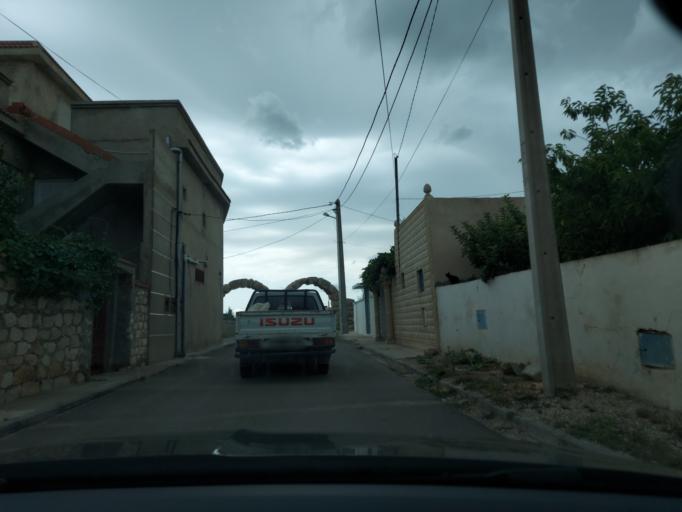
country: TN
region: Silyanah
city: Maktar
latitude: 35.8533
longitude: 9.1973
